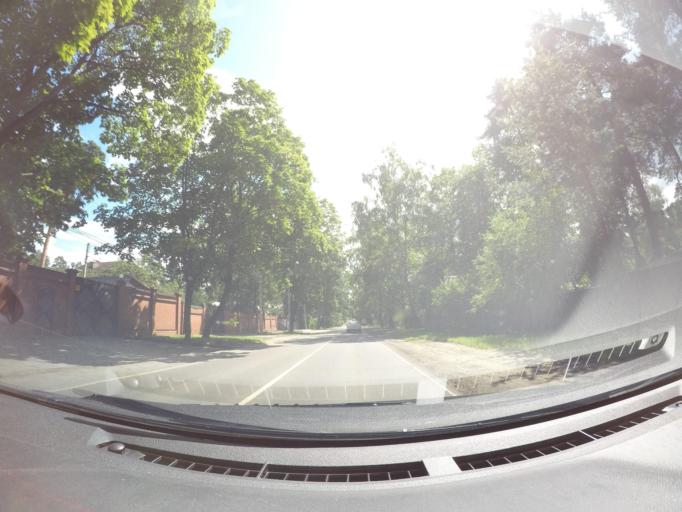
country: RU
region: Moskovskaya
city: Kraskovo
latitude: 55.6517
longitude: 37.9965
